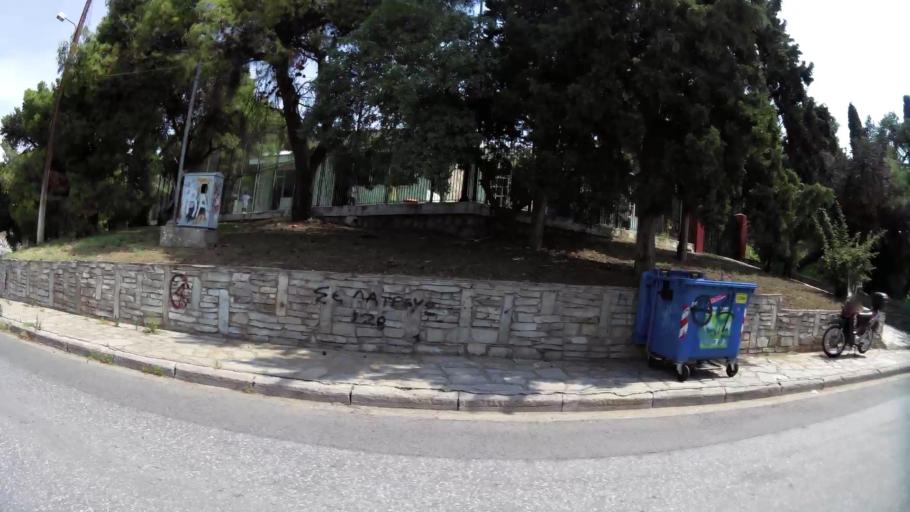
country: GR
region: Central Macedonia
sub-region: Nomos Thessalonikis
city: Agios Pavlos
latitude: 40.6373
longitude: 22.9643
